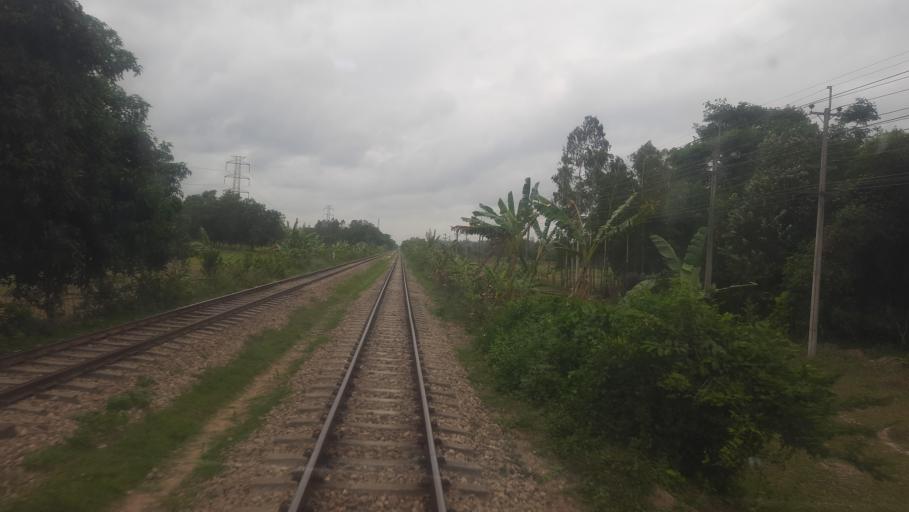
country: BD
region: Chittagong
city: Fatikchari
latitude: 22.7867
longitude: 91.5825
